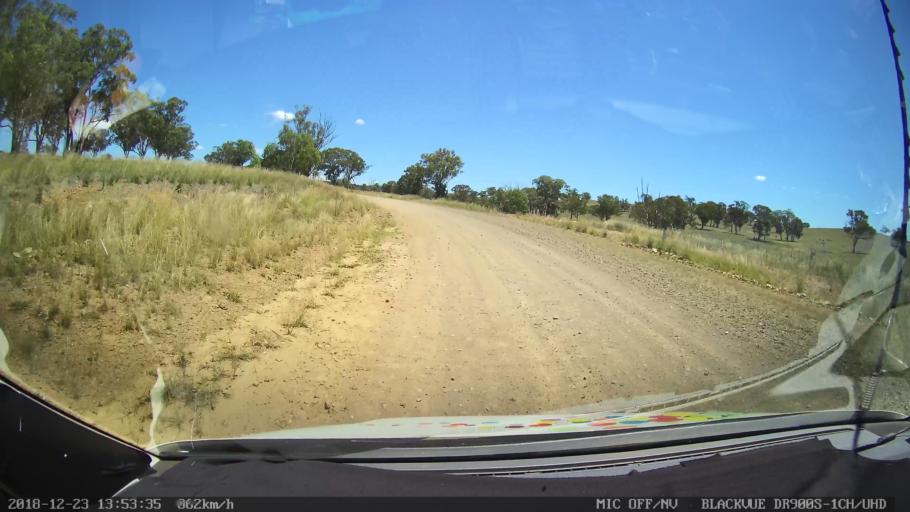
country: AU
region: New South Wales
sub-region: Tamworth Municipality
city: Manilla
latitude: -30.5537
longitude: 151.0933
